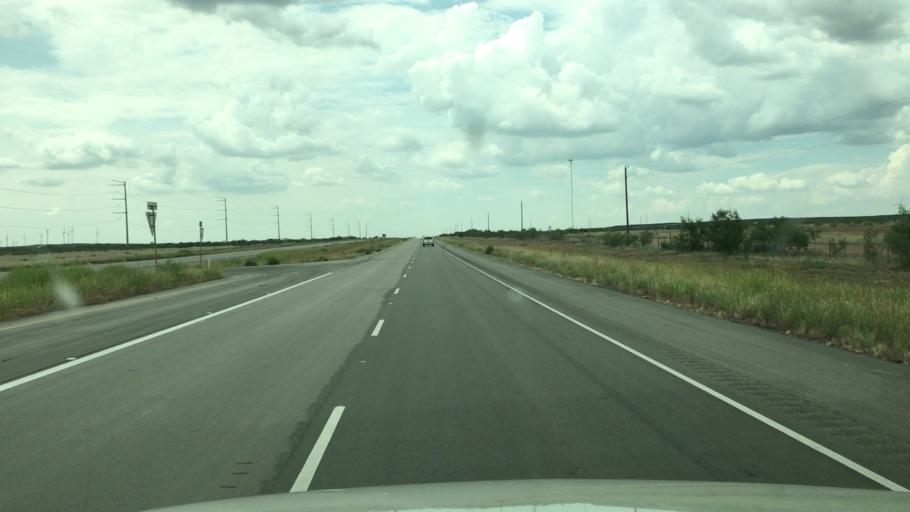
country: US
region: Texas
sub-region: Glasscock County
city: Garden City
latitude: 31.9738
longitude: -101.2458
